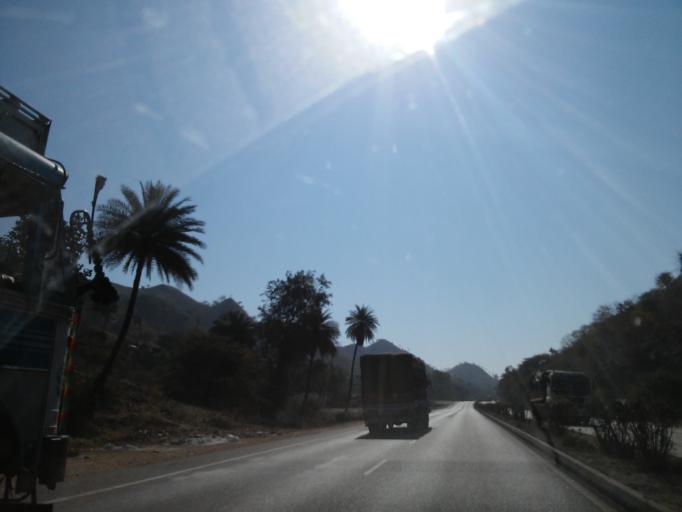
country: IN
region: Rajasthan
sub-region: Udaipur
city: Udaipur
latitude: 24.3200
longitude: 73.6749
